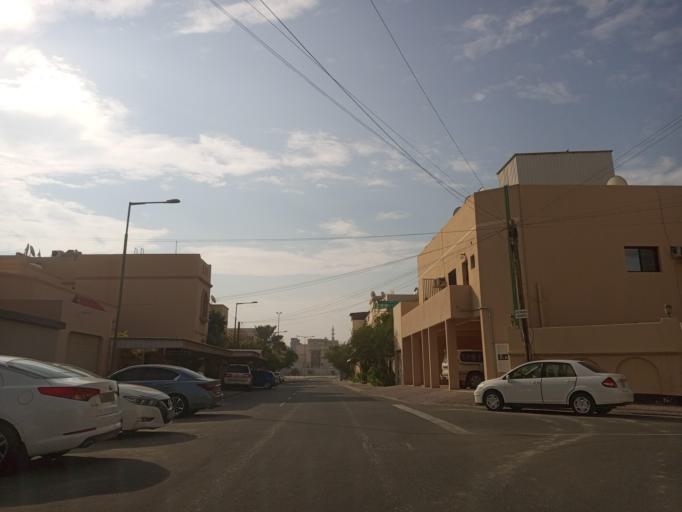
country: BH
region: Muharraq
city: Al Hadd
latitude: 26.2486
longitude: 50.6443
